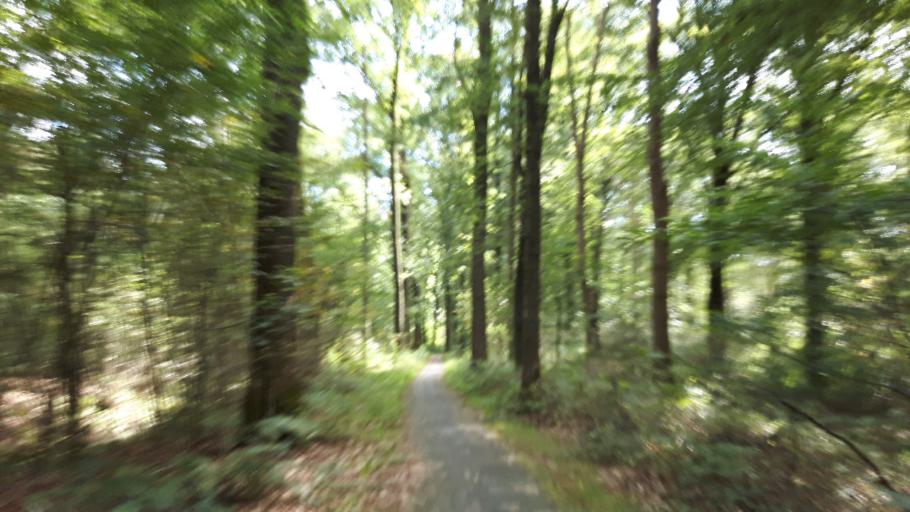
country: NL
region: Friesland
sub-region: Gemeente Smallingerland
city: Drachtstercompagnie
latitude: 53.0696
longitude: 6.2052
